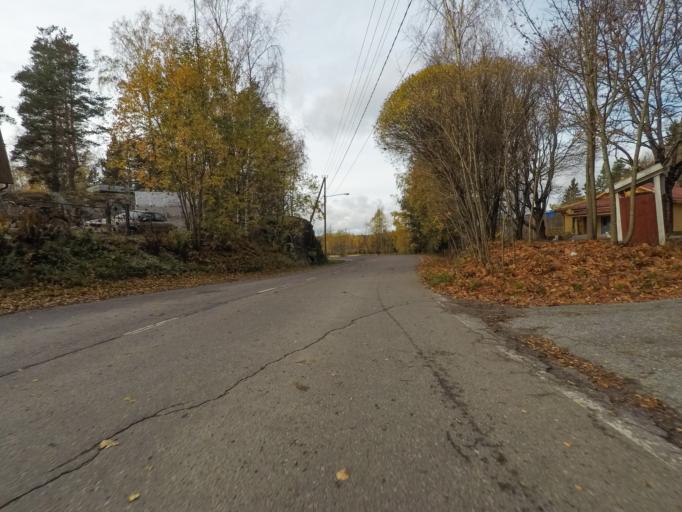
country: FI
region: Uusimaa
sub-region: Helsinki
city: Vantaa
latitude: 60.2565
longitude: 25.1394
